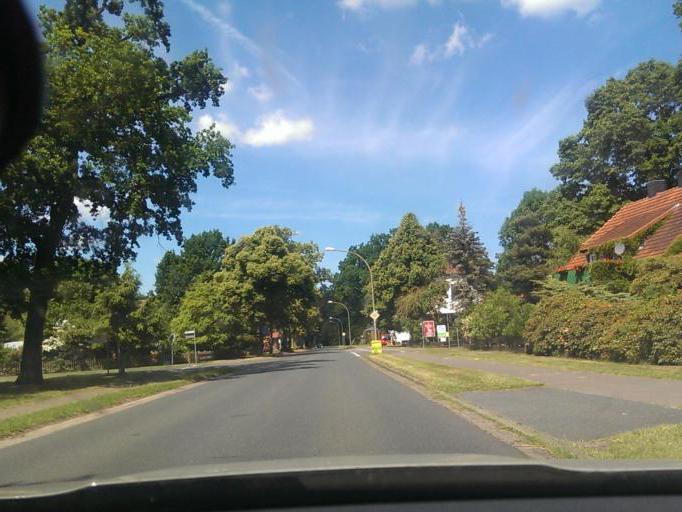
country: DE
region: Lower Saxony
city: Hellwege
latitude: 53.0732
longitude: 9.2398
